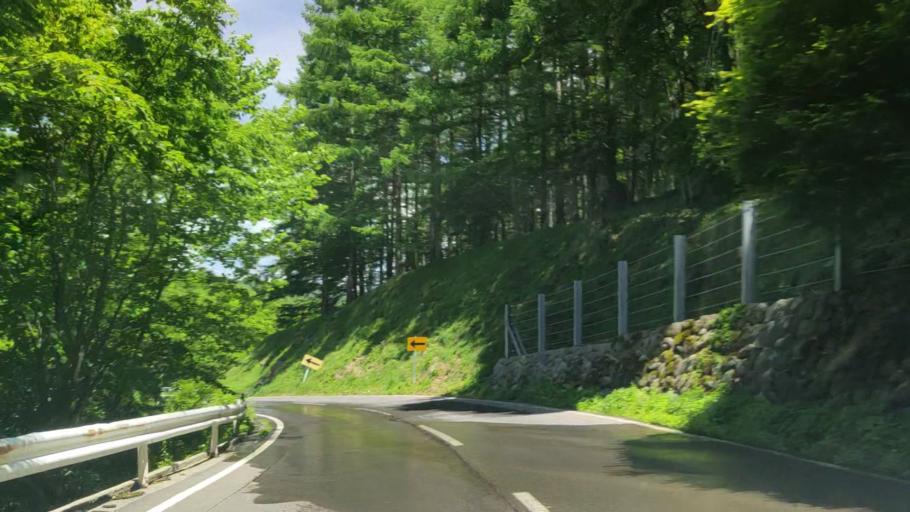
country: JP
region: Nagano
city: Kamimaruko
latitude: 36.1566
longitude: 138.2399
